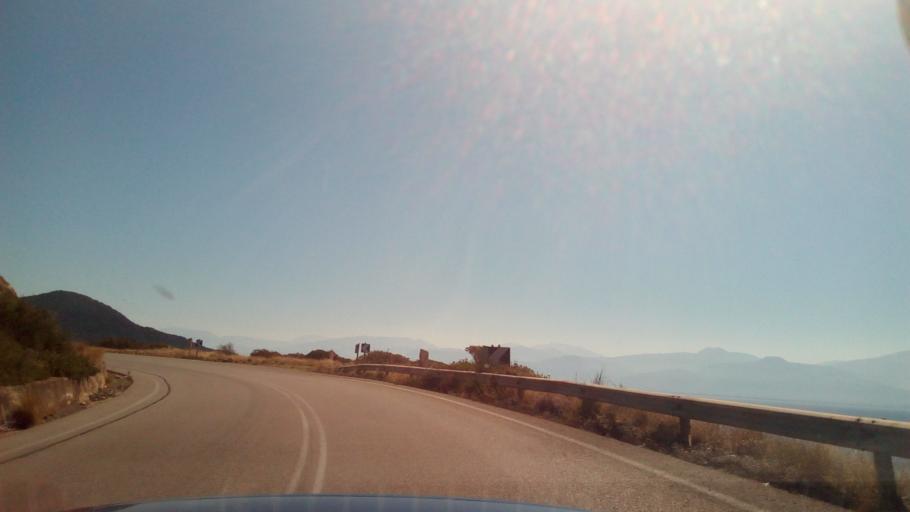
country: GR
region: West Greece
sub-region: Nomos Achaias
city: Aigio
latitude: 38.3605
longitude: 22.1280
